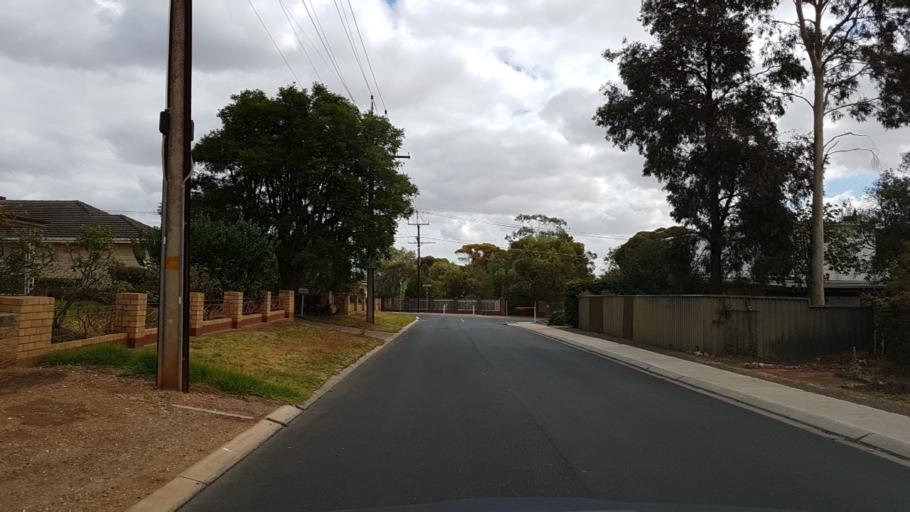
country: AU
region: South Australia
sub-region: Gawler
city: Gawler
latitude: -34.6045
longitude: 138.7548
